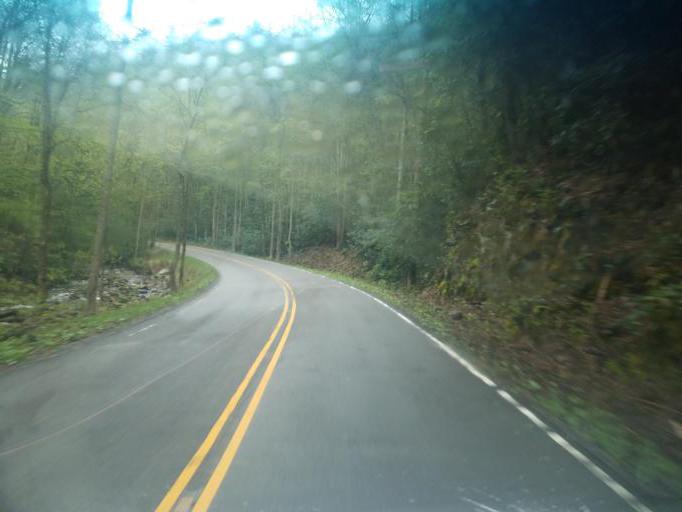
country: US
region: Virginia
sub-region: Washington County
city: Glade Spring
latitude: 36.6450
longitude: -81.7215
